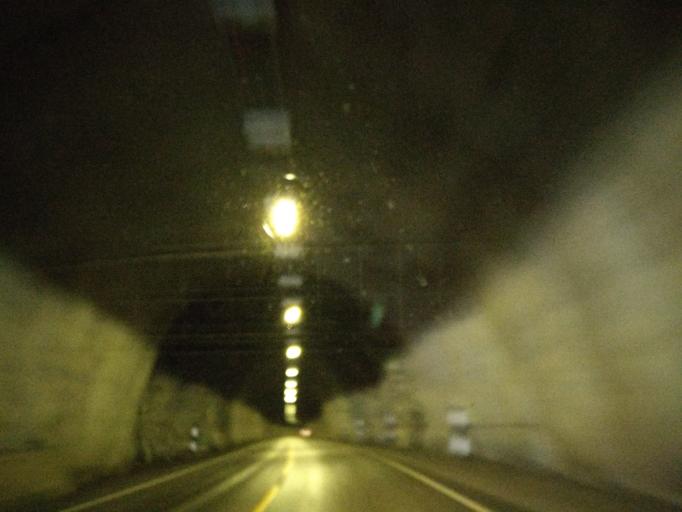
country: NO
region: Rogaland
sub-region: Forsand
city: Forsand
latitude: 58.7872
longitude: 6.2885
